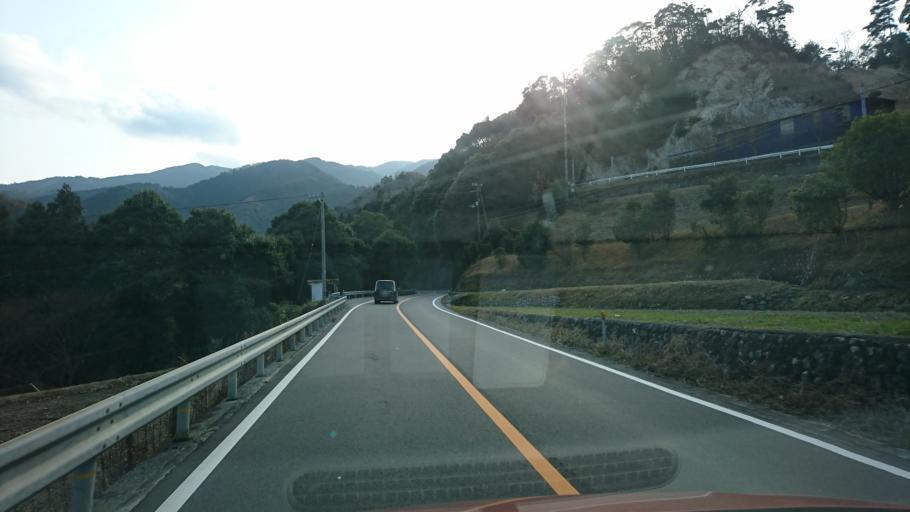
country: JP
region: Ehime
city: Hojo
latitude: 33.9744
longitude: 132.9032
